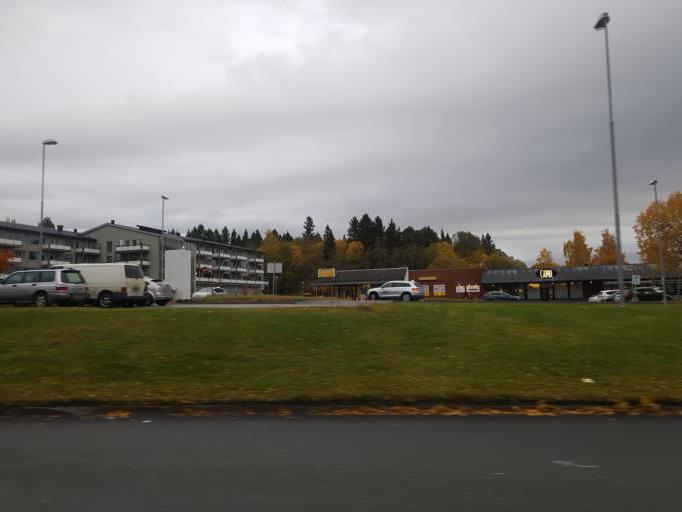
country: NO
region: Sor-Trondelag
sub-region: Trondheim
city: Trondheim
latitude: 63.3730
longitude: 10.3458
